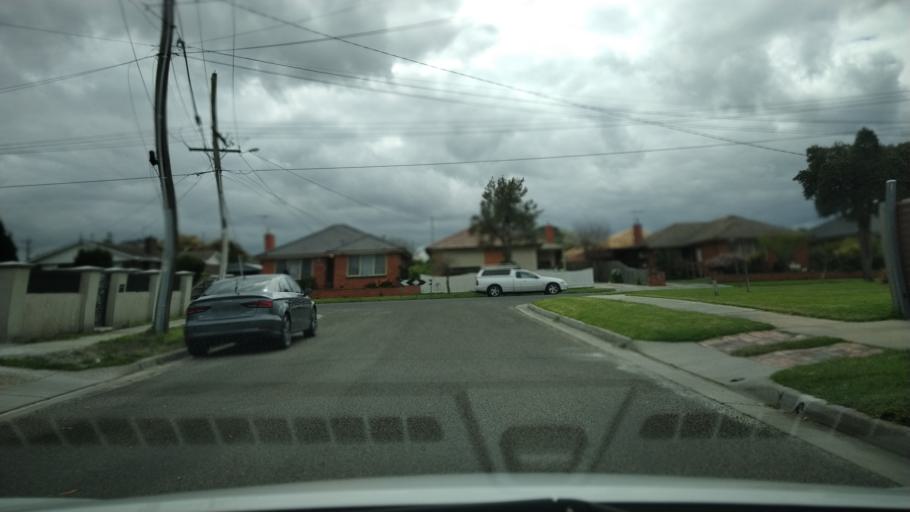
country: AU
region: Victoria
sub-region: Greater Dandenong
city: Noble Park
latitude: -37.9760
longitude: 145.1792
